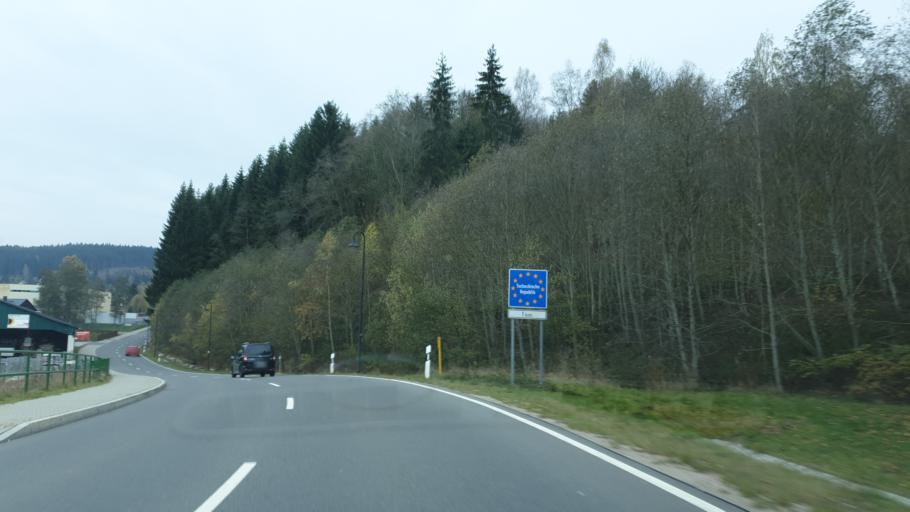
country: DE
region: Saxony
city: Johanngeorgenstadt
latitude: 50.4359
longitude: 12.7280
